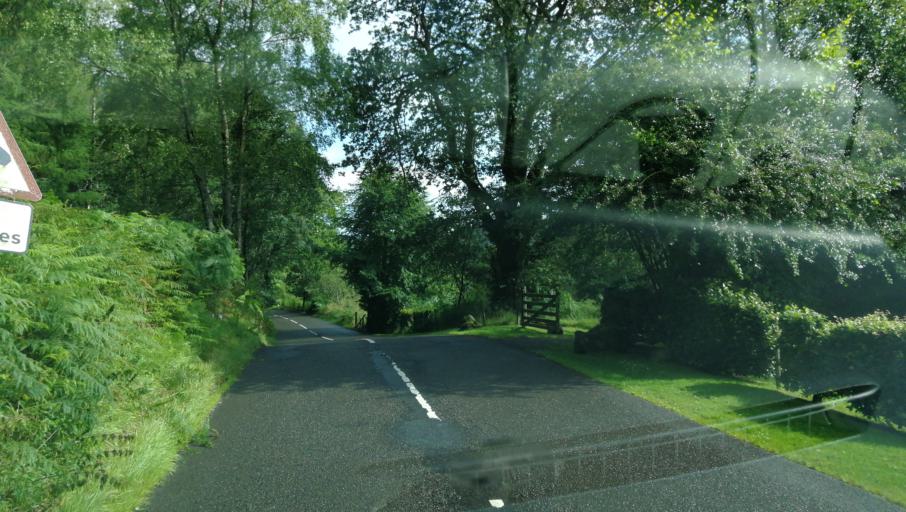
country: GB
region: Scotland
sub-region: Stirling
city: Balfron
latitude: 56.2311
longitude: -4.4005
